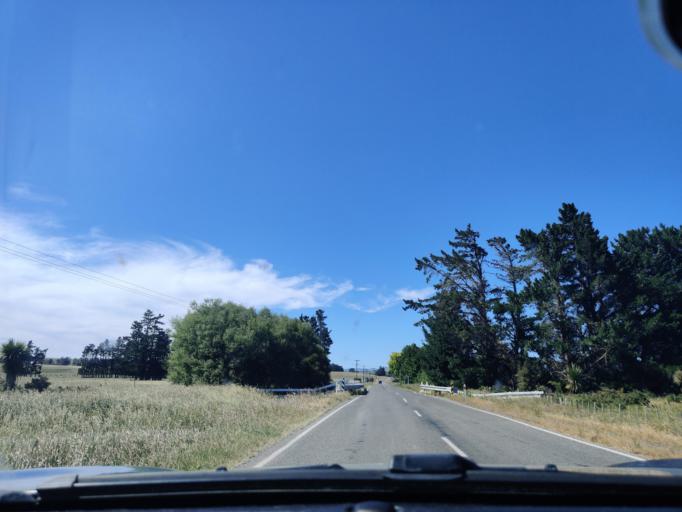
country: NZ
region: Wellington
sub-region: South Wairarapa District
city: Waipawa
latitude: -41.1917
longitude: 175.3596
